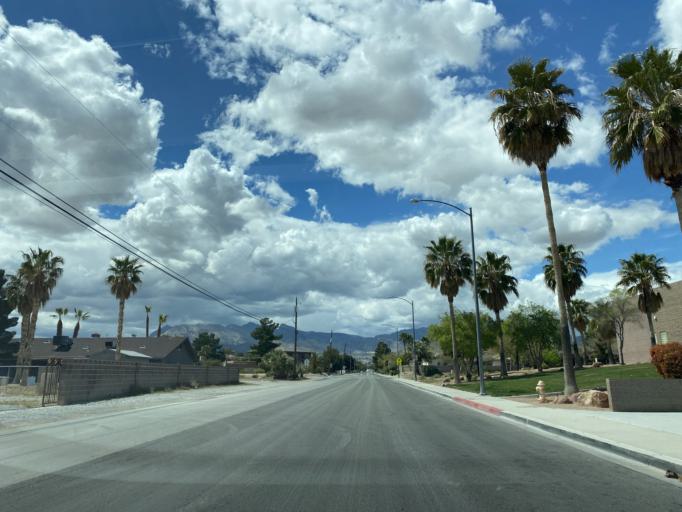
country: US
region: Nevada
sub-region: Clark County
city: Spring Valley
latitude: 36.2443
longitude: -115.2638
